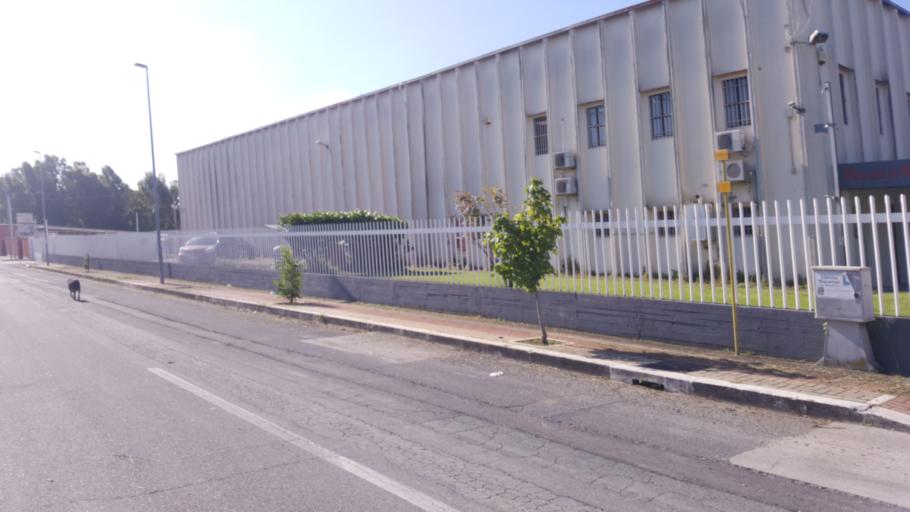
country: IT
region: Latium
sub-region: Provincia di Latina
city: Aprilia
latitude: 41.5742
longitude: 12.6467
